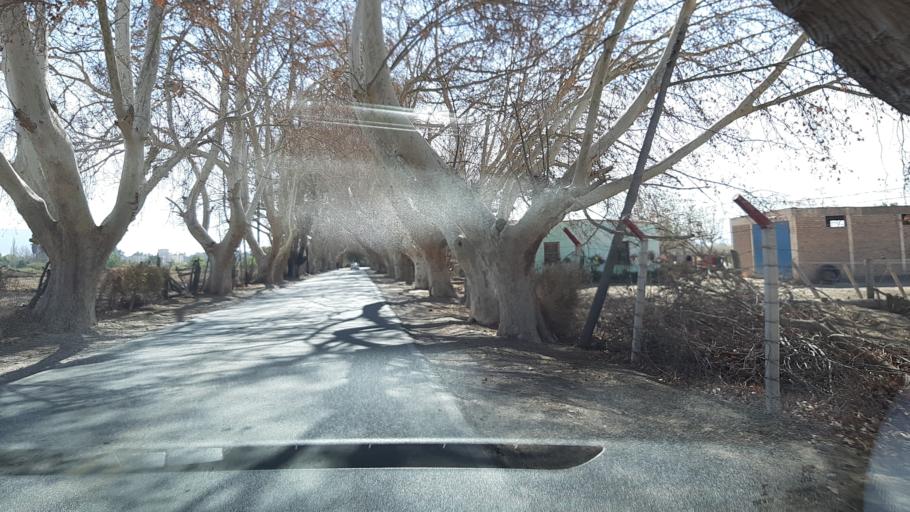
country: AR
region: San Juan
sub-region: Departamento de Rivadavia
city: Rivadavia
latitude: -31.5295
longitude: -68.6189
